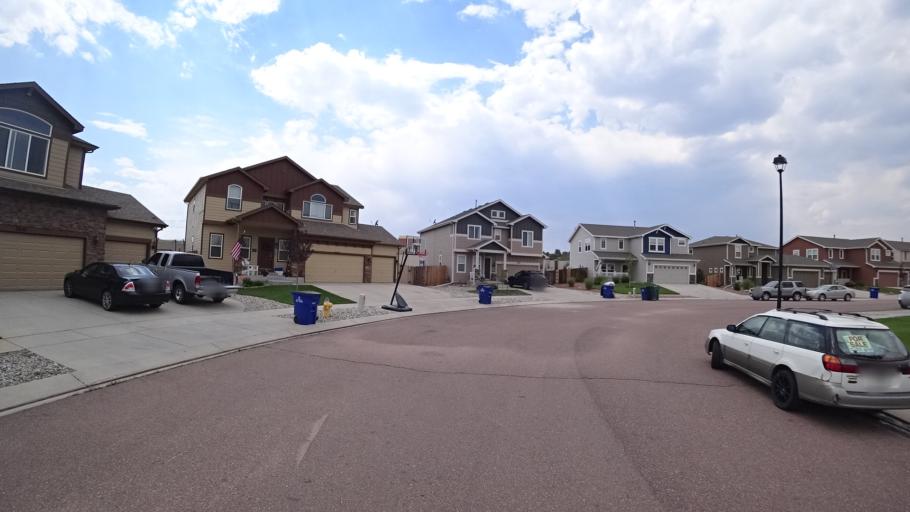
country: US
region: Colorado
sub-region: El Paso County
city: Black Forest
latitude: 38.9442
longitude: -104.7000
